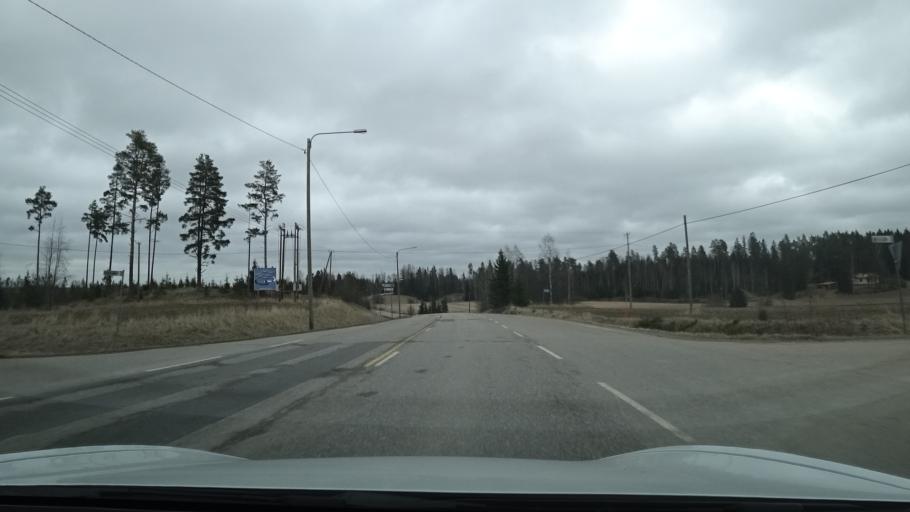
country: FI
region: Uusimaa
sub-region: Porvoo
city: Pukkila
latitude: 60.6535
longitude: 25.6707
